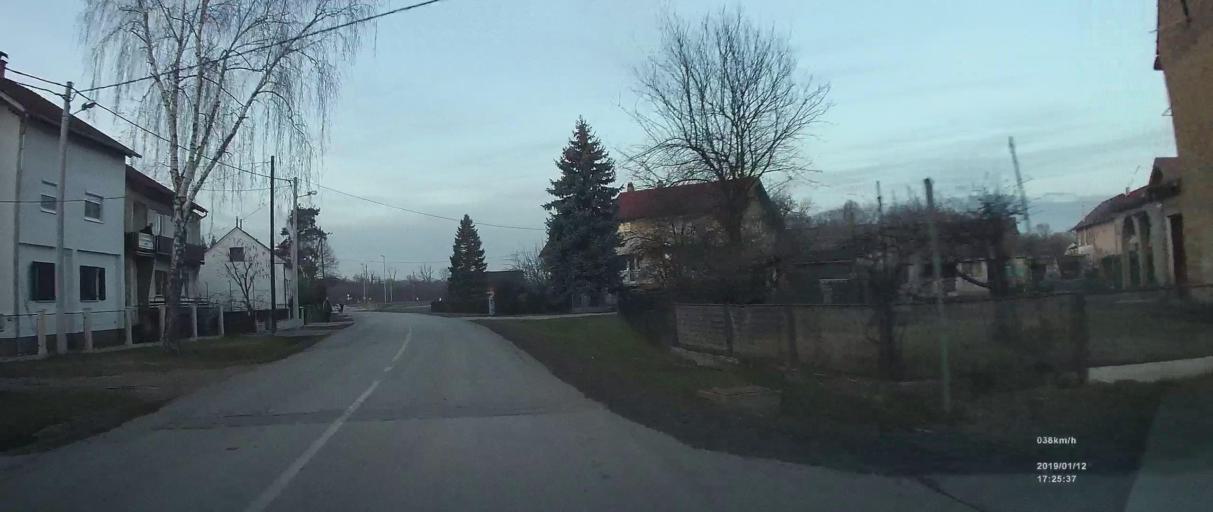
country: HR
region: Zagrebacka
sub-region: Grad Velika Gorica
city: Velika Gorica
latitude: 45.7327
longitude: 16.1014
